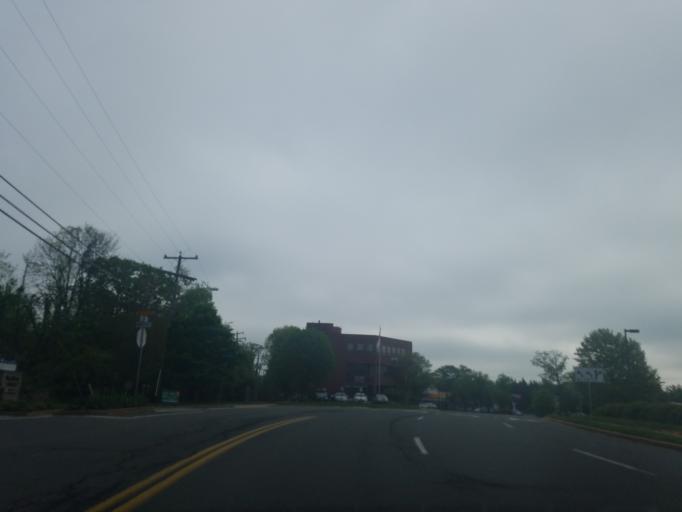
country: US
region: Virginia
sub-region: Fairfax County
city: Dunn Loring
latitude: 38.9004
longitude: -77.2259
